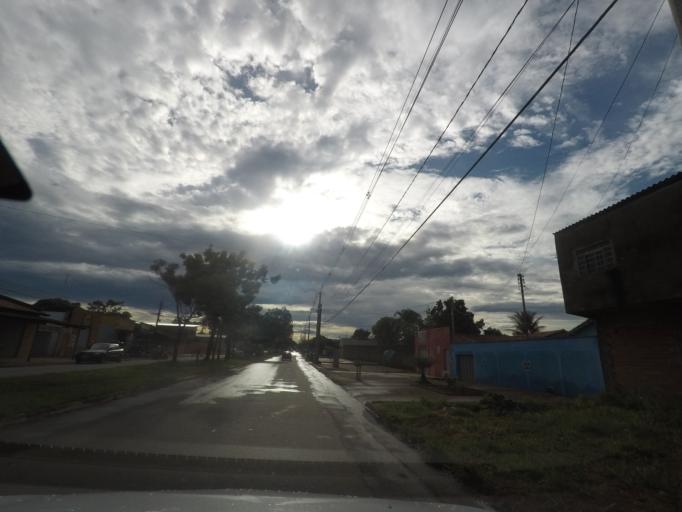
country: BR
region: Goias
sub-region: Aparecida De Goiania
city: Aparecida de Goiania
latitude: -16.7611
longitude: -49.3544
